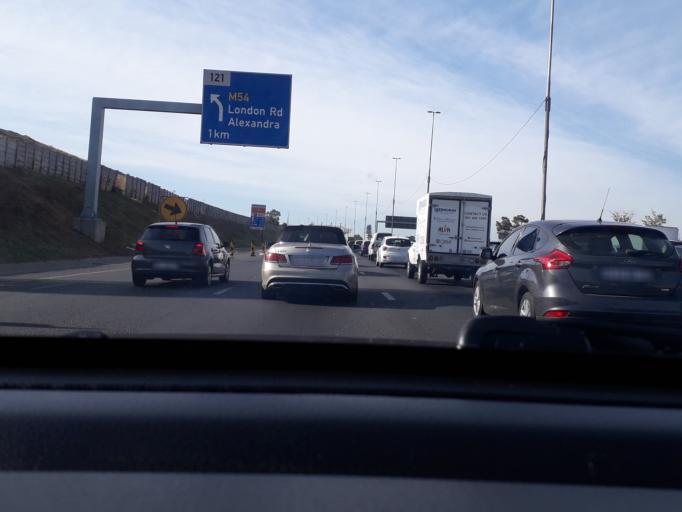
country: ZA
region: Gauteng
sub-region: City of Johannesburg Metropolitan Municipality
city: Modderfontein
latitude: -26.0893
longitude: 28.1163
